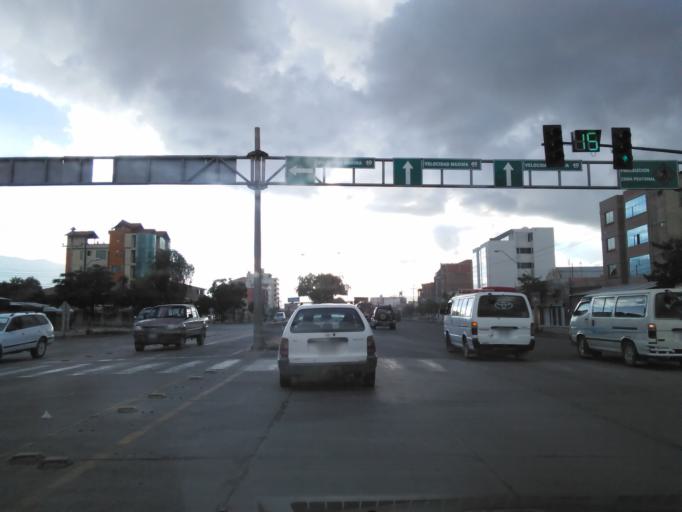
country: BO
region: Cochabamba
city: Cochabamba
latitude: -17.3927
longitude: -66.1994
